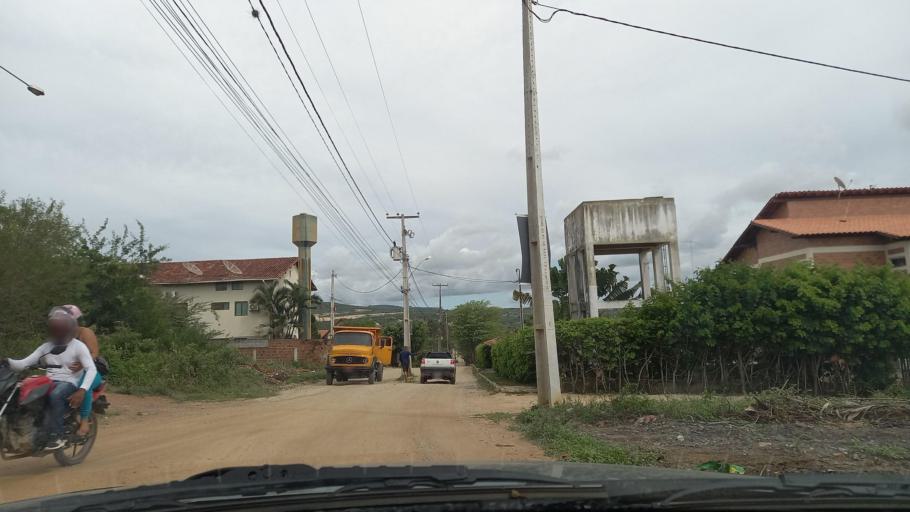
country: BR
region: Pernambuco
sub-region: Gravata
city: Gravata
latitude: -8.1945
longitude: -35.6002
